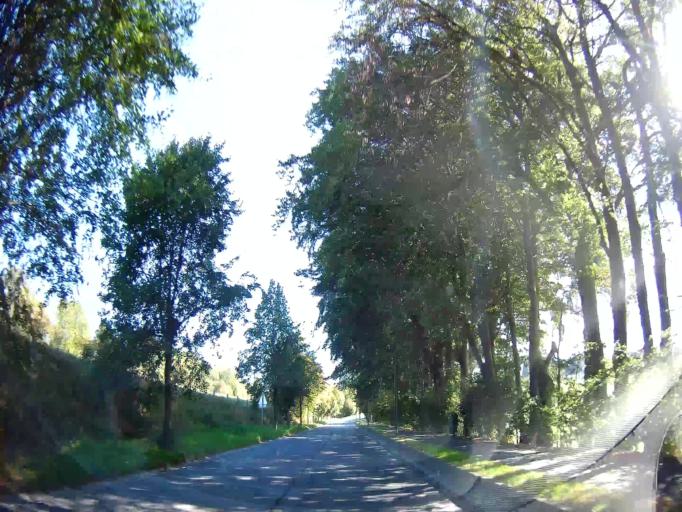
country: BE
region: Wallonia
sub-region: Province du Luxembourg
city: Bastogne
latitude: 50.0096
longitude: 5.7327
